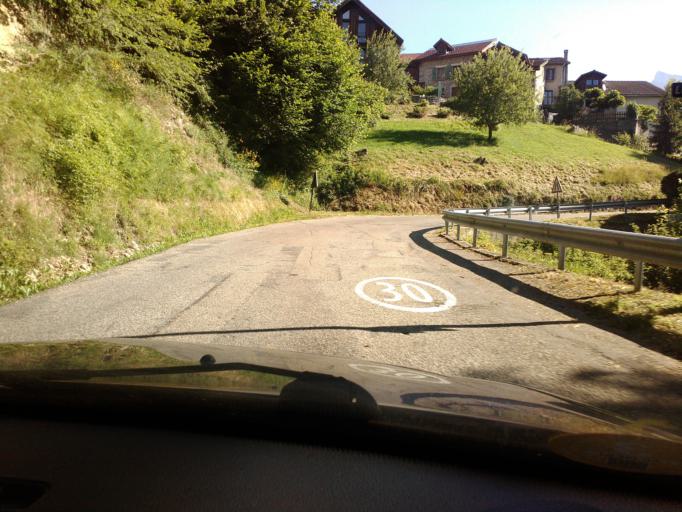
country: FR
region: Rhone-Alpes
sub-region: Departement de l'Isere
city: Saint-Egreve
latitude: 45.2570
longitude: 5.6946
